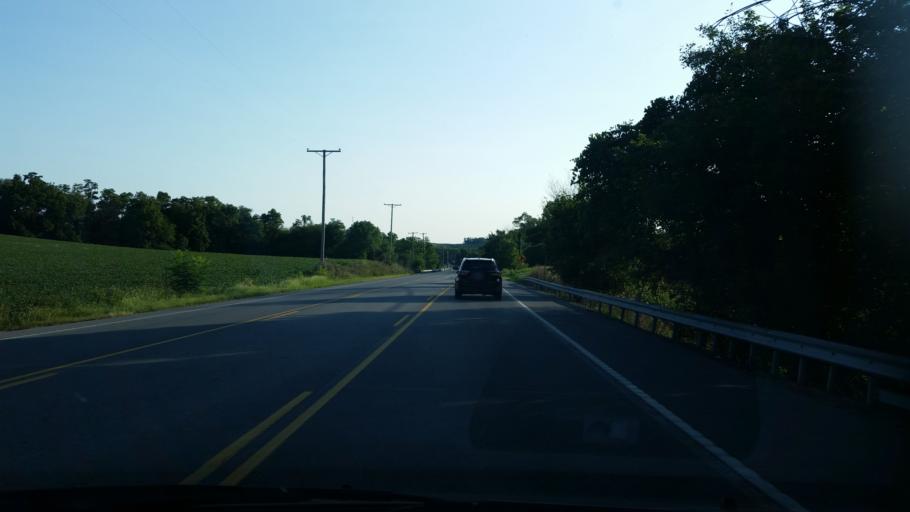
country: US
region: Pennsylvania
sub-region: Blair County
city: Bellwood
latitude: 40.6088
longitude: -78.3139
